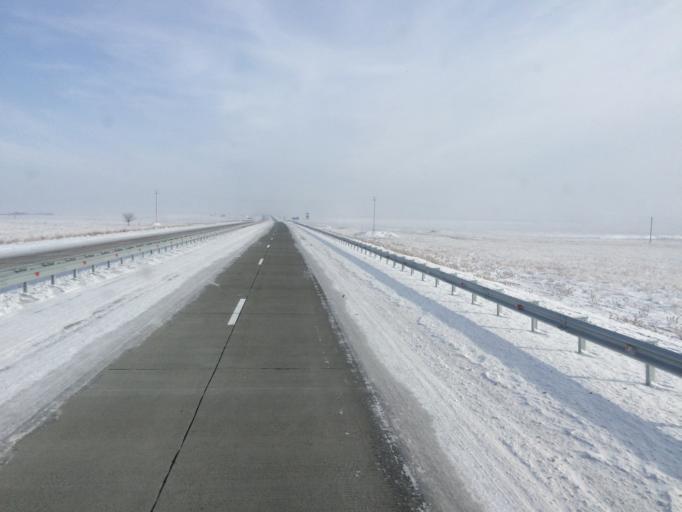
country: KZ
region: Zhambyl
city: Georgiyevka
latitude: 43.3424
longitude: 74.4059
